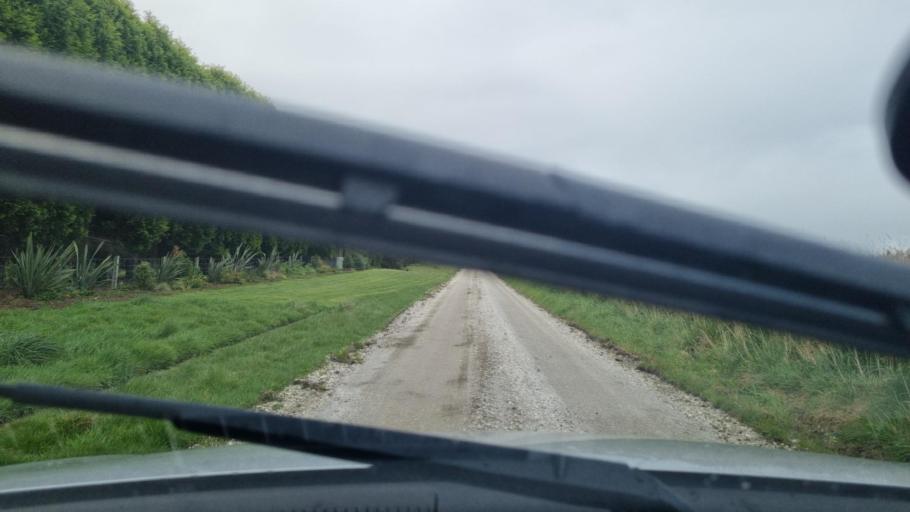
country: NZ
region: Southland
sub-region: Invercargill City
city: Invercargill
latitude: -46.4960
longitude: 168.4196
